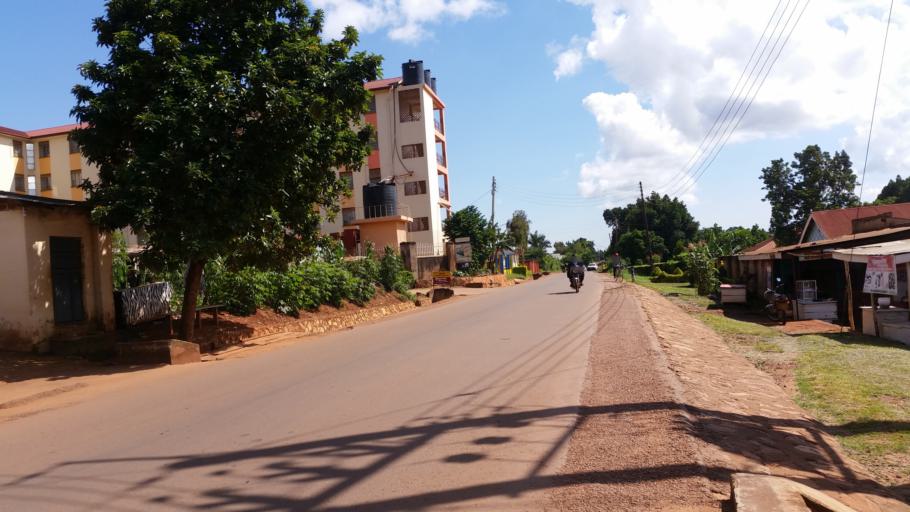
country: UG
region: Central Region
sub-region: Wakiso District
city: Kireka
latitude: 0.3539
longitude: 32.6369
